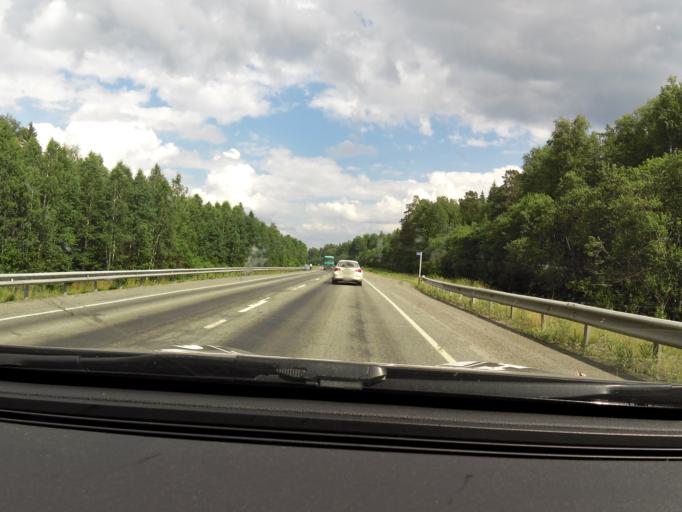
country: RU
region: Sverdlovsk
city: Bisert'
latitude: 56.8323
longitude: 58.8102
